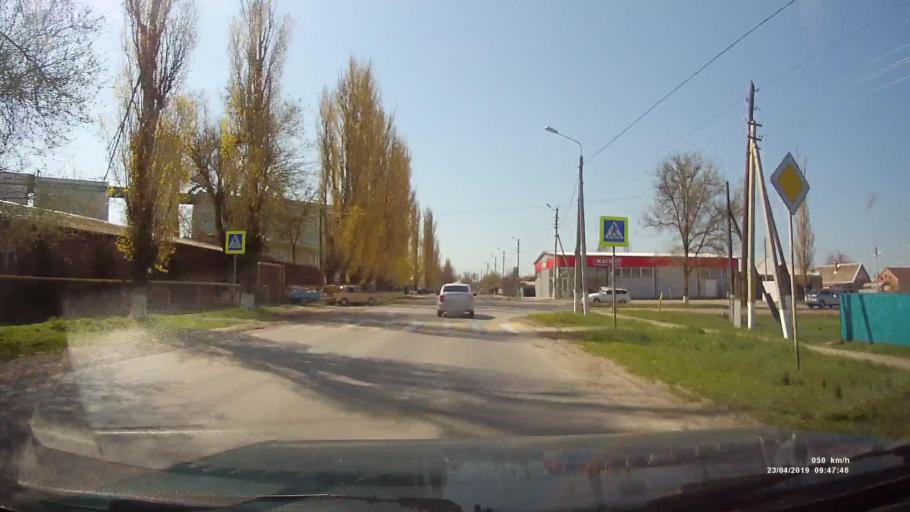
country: RU
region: Rostov
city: Orlovskiy
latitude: 46.8729
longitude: 42.0384
